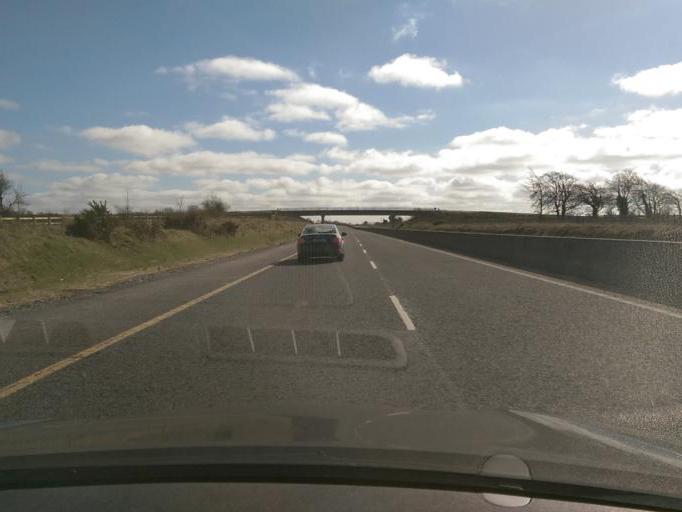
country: IE
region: Leinster
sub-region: An Iarmhi
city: Kilbeggan
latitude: 53.3742
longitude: -7.5488
